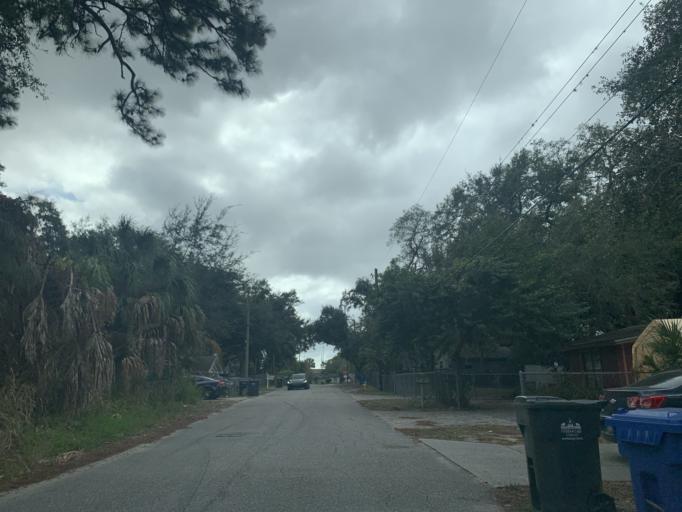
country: US
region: Florida
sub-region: Hillsborough County
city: East Lake-Orient Park
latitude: 27.9788
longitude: -82.3912
